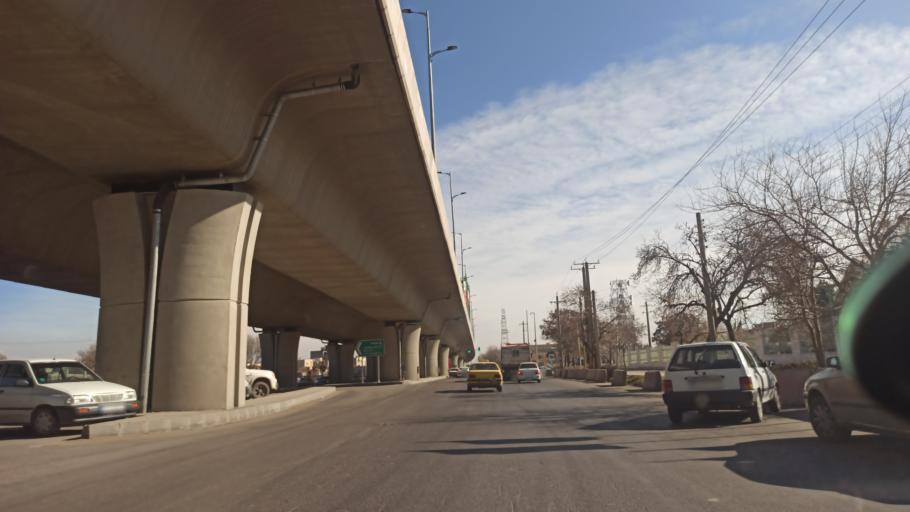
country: IR
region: Qazvin
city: Qazvin
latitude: 36.2551
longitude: 49.9995
